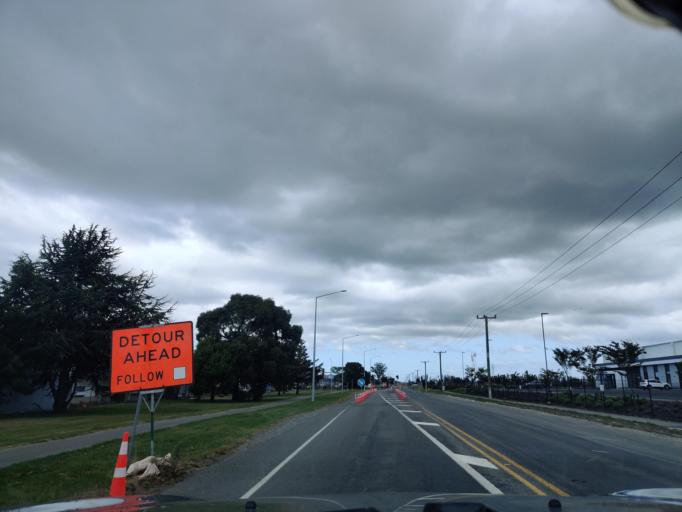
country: NZ
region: Canterbury
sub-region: Selwyn District
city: Prebbleton
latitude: -43.5543
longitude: 172.5135
